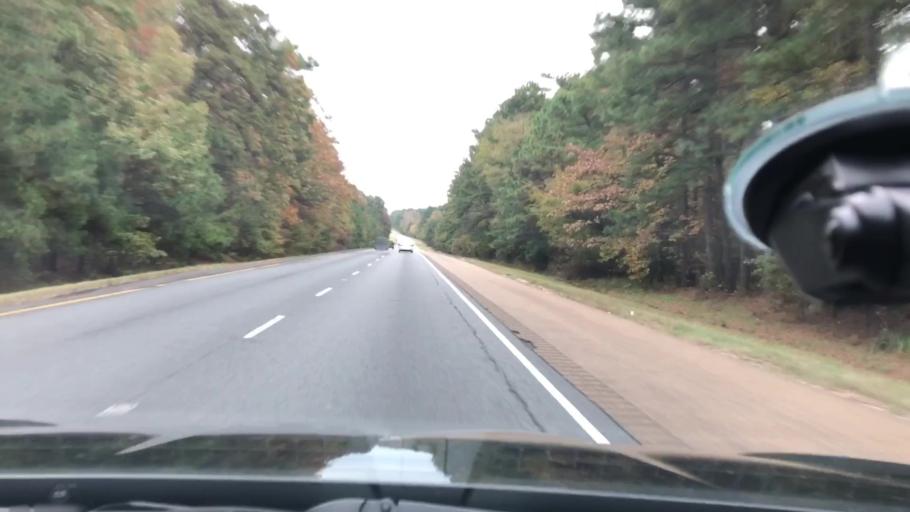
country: US
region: Arkansas
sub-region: Clark County
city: Gurdon
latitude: 33.9406
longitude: -93.2454
